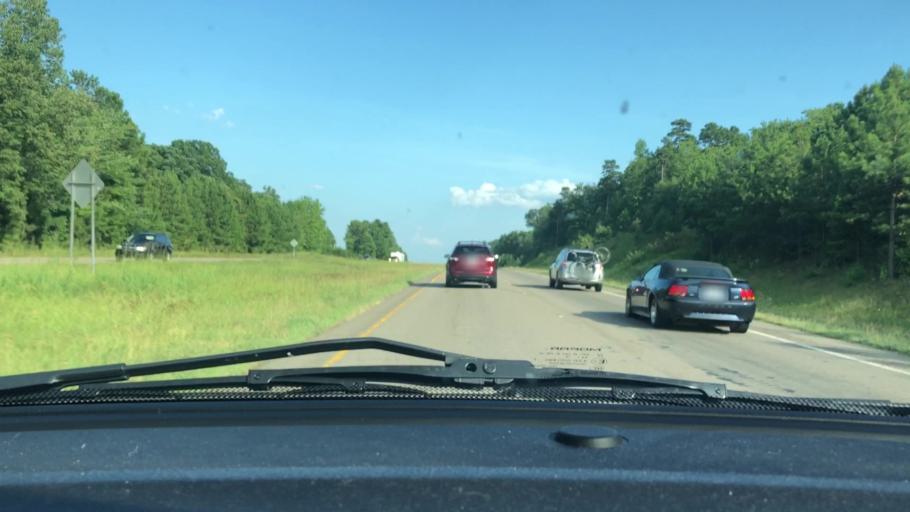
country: US
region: North Carolina
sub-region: Chatham County
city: Siler City
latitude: 35.6301
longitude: -79.3675
